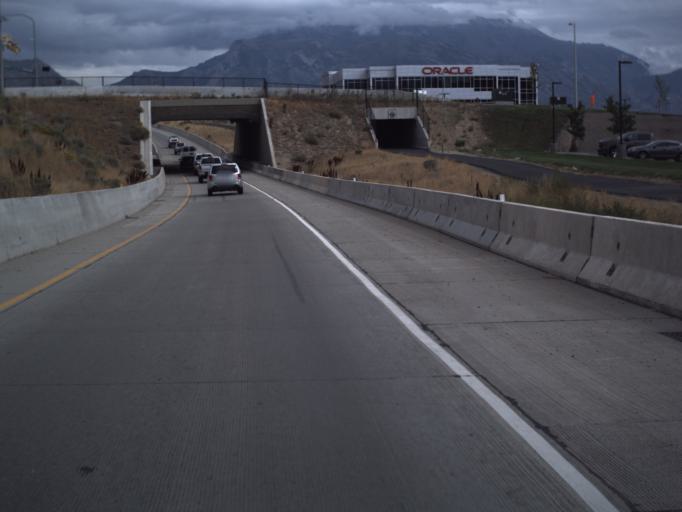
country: US
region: Utah
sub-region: Utah County
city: Lehi
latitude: 40.4313
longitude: -111.8826
